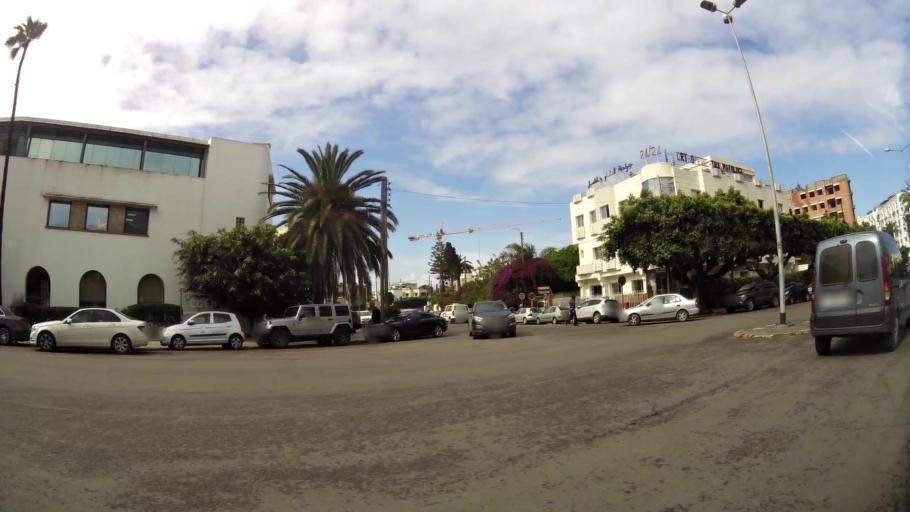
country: MA
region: Grand Casablanca
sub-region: Casablanca
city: Casablanca
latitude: 33.5822
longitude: -7.6277
